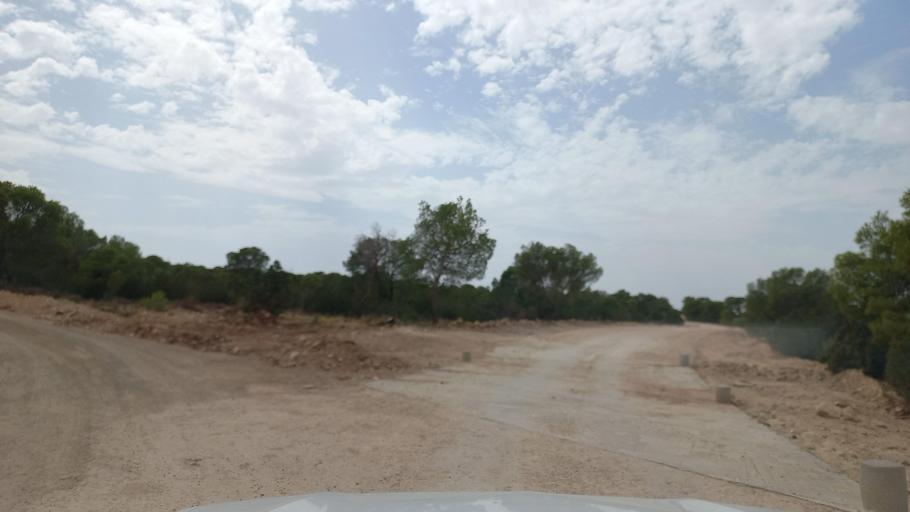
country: TN
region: Al Qasrayn
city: Kasserine
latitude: 35.3815
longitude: 8.8806
